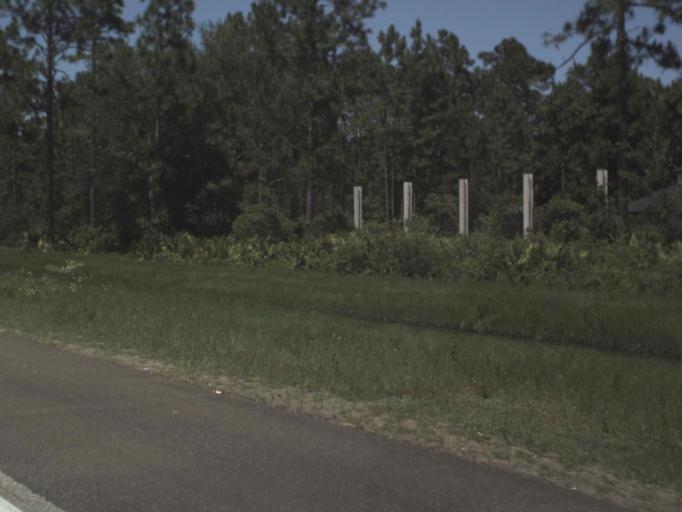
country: US
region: Florida
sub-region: Clay County
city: Bellair-Meadowbrook Terrace
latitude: 30.2383
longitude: -81.8437
